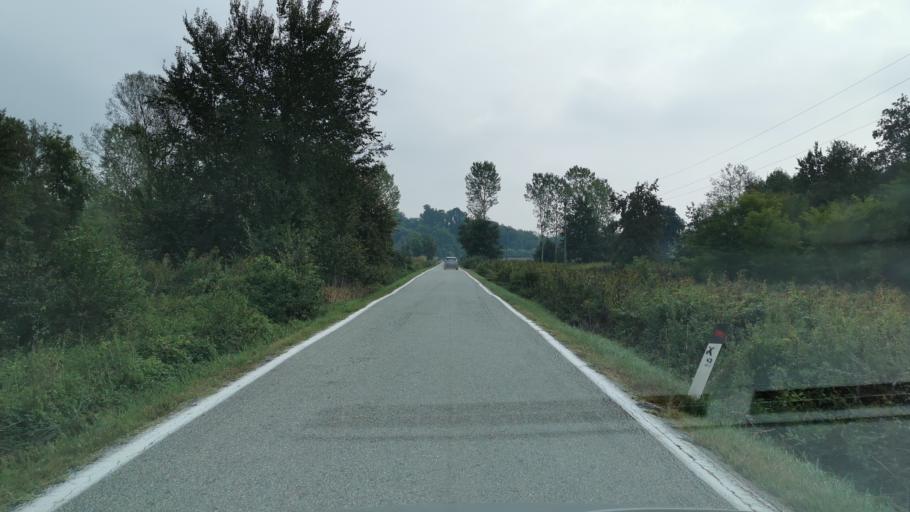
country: IT
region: Piedmont
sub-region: Provincia di Torino
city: Montanaro
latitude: 45.2486
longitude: 7.8349
